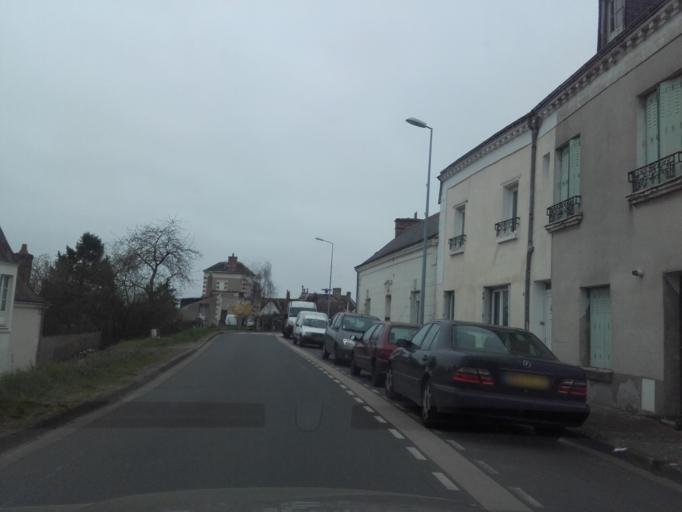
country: FR
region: Centre
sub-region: Departement d'Indre-et-Loire
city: Fondettes
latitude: 47.3783
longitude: 0.6008
